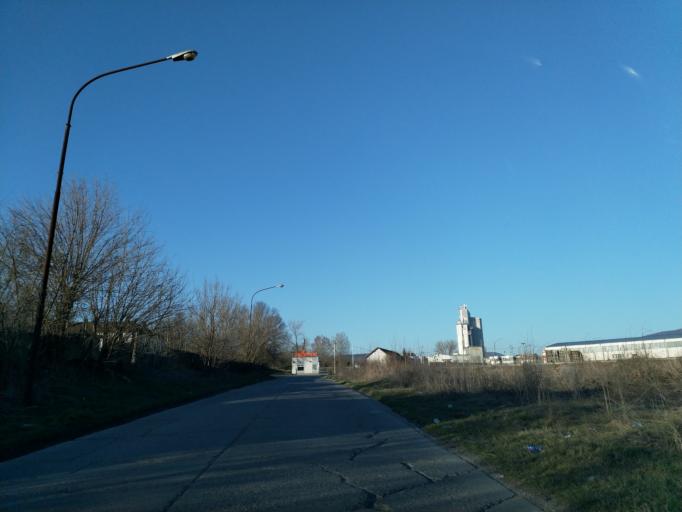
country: RS
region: Central Serbia
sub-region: Pomoravski Okrug
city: Paracin
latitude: 43.9023
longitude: 21.4954
